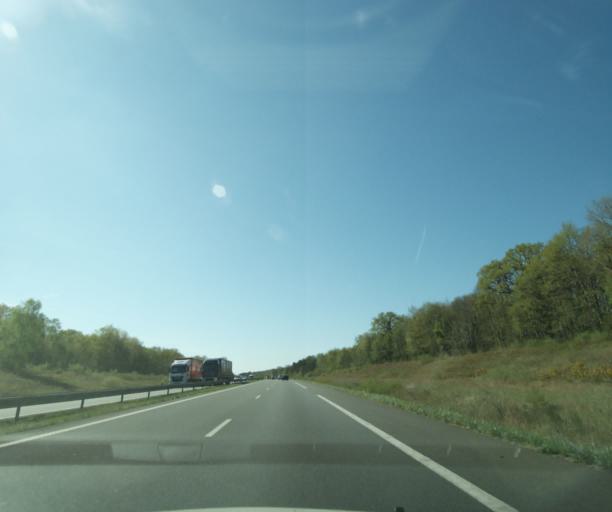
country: FR
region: Centre
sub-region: Departement du Loir-et-Cher
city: Nouan-le-Fuzelier
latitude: 47.5010
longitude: 2.0067
